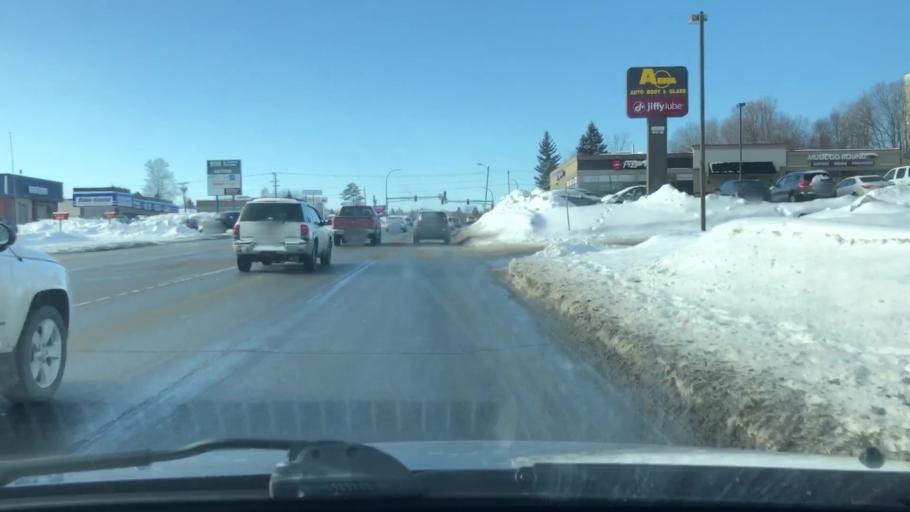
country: US
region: Minnesota
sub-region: Saint Louis County
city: Duluth
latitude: 46.8005
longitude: -92.1296
